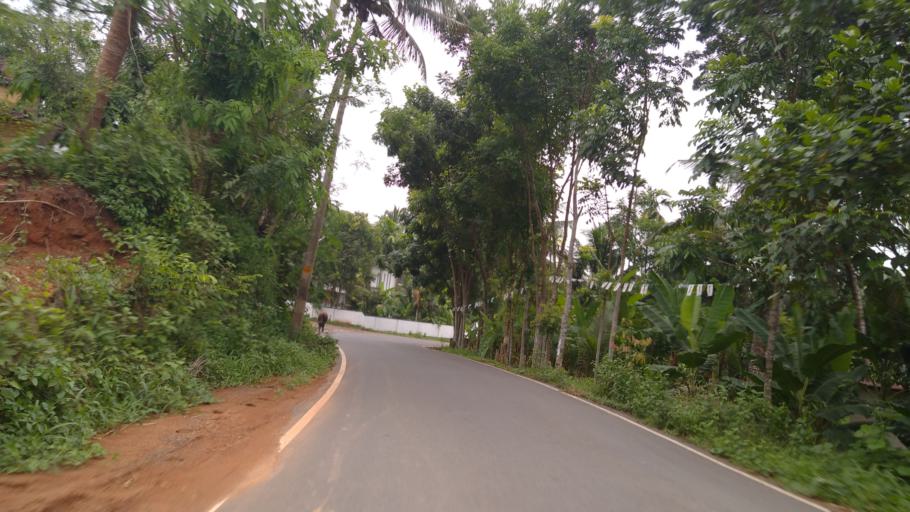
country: IN
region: Kerala
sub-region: Ernakulam
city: Perumbavoor
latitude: 10.0267
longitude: 76.4904
